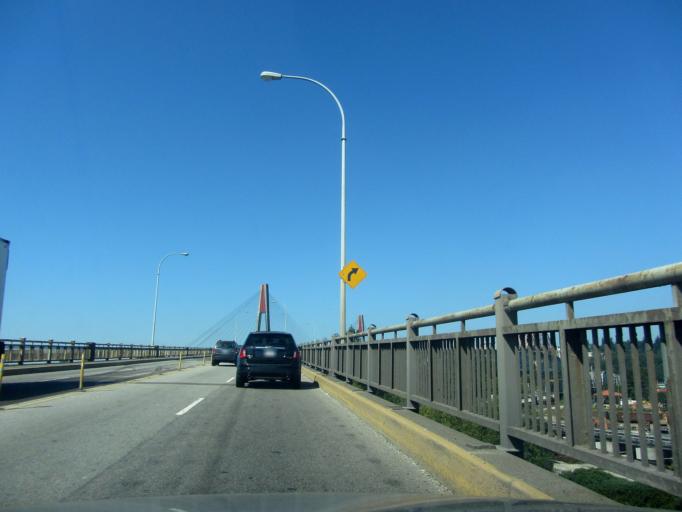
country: CA
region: British Columbia
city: New Westminster
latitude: 49.2058
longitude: -122.8838
